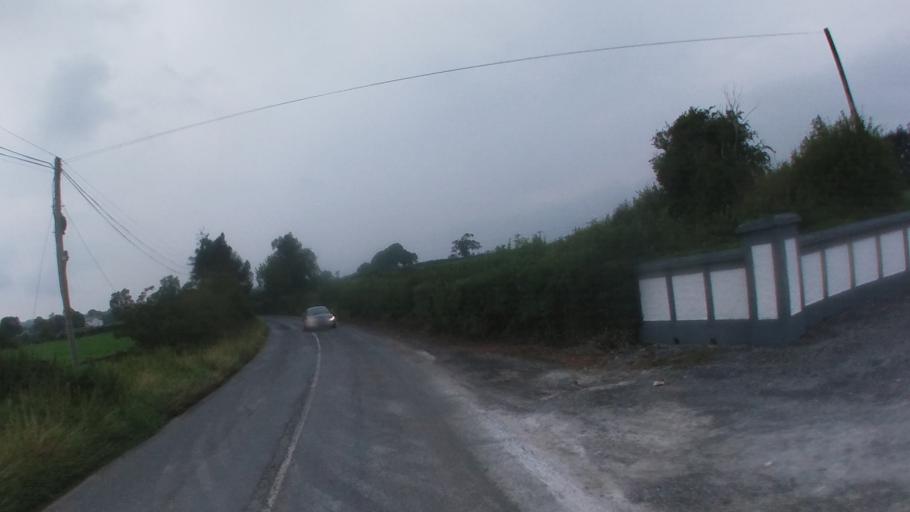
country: IE
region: Munster
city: Fethard
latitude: 52.4656
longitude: -7.6925
